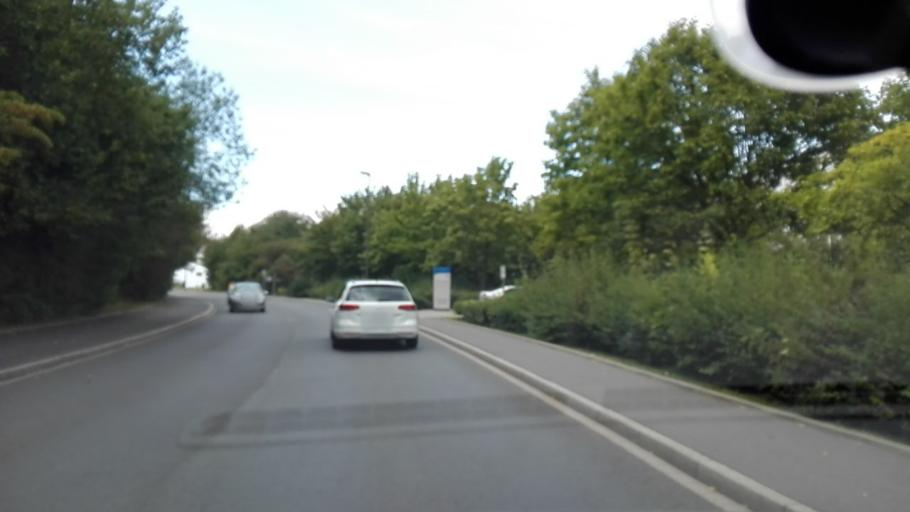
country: DE
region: North Rhine-Westphalia
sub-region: Regierungsbezirk Arnsberg
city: Dortmund
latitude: 51.4934
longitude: 7.4296
